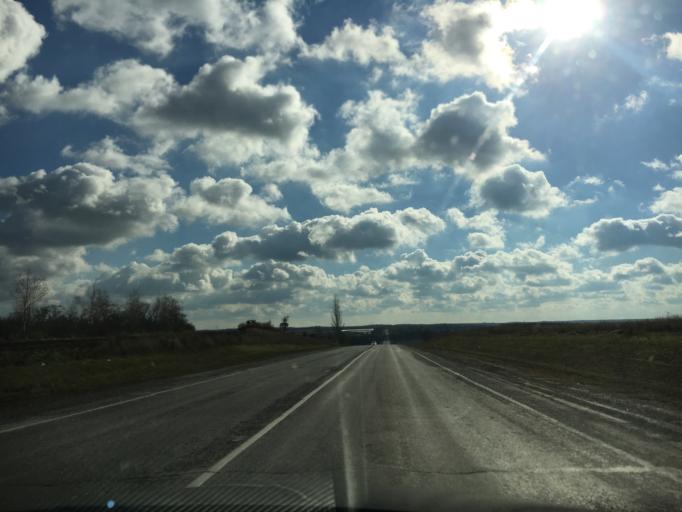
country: RU
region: Rostov
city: Matveyev Kurgan
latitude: 47.5122
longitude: 38.9025
